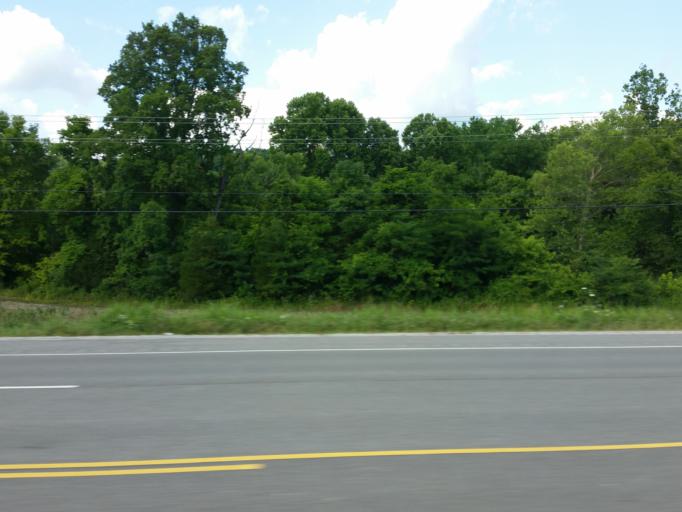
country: US
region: Tennessee
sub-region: Lewis County
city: Hohenwald
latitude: 35.5720
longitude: -87.4257
